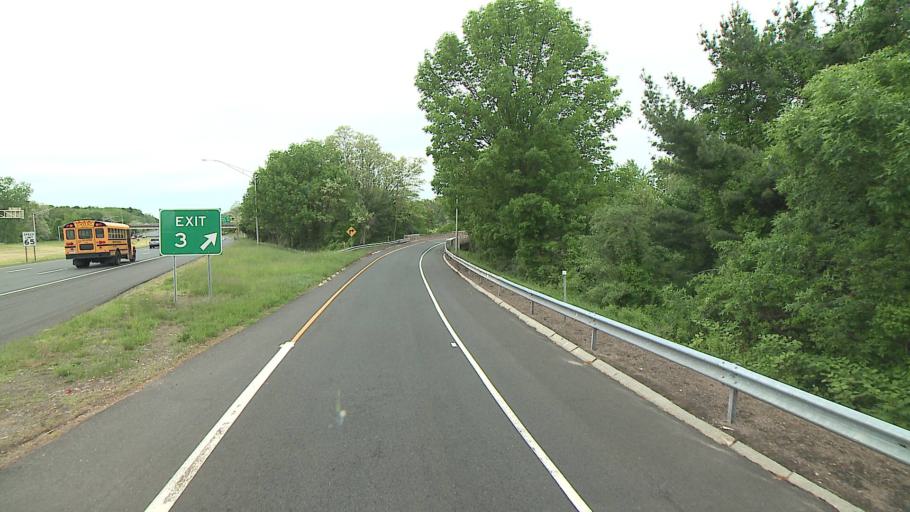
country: US
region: Connecticut
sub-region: Hartford County
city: Manchester
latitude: 41.7625
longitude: -72.5163
